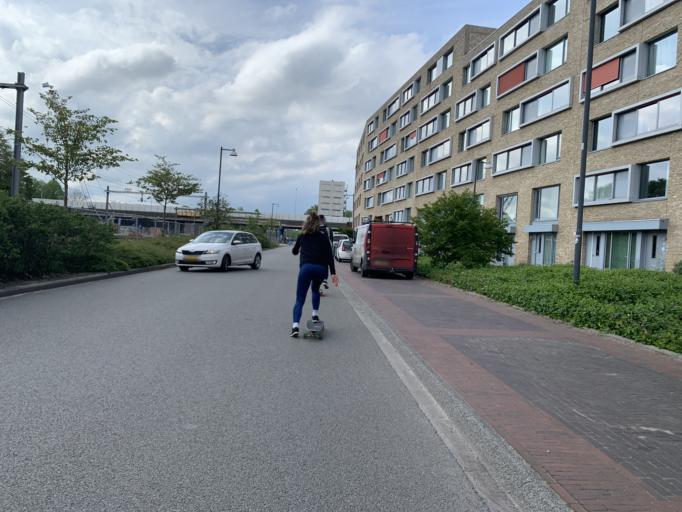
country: NL
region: Groningen
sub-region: Gemeente Groningen
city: Oosterpark
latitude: 53.2068
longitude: 6.5820
